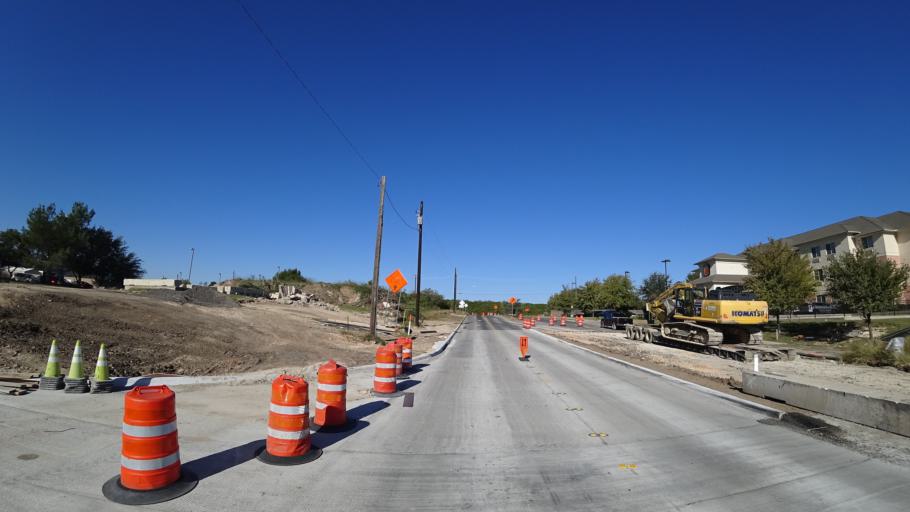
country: US
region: Texas
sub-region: Travis County
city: Austin
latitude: 30.2924
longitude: -97.6641
